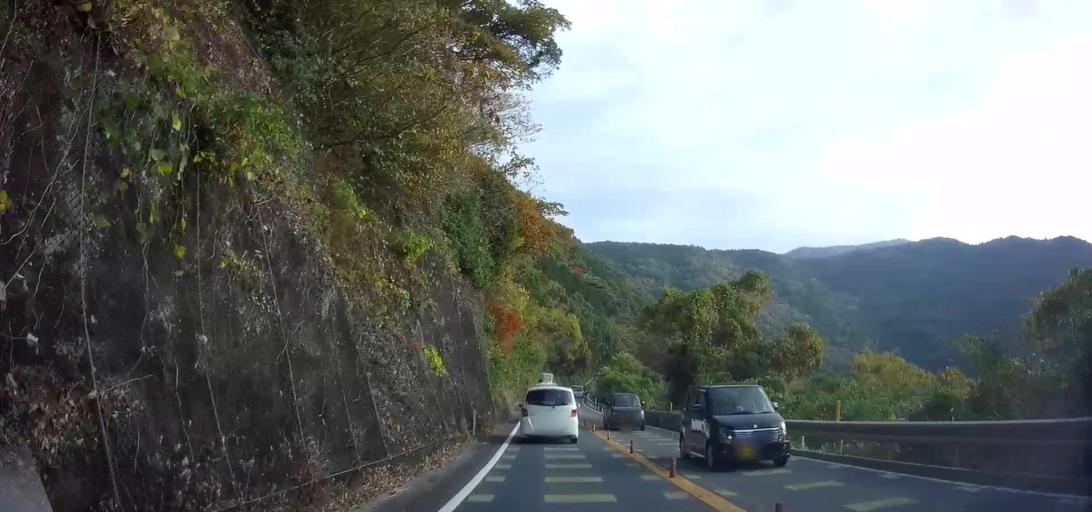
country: JP
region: Nagasaki
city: Shimabara
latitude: 32.7567
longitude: 130.2050
